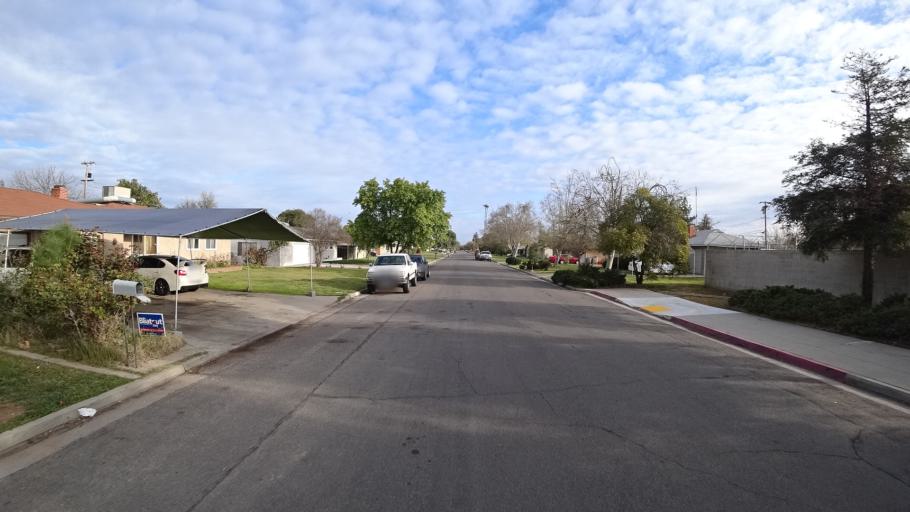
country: US
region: California
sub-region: Fresno County
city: Fresno
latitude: 36.8252
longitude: -119.7926
